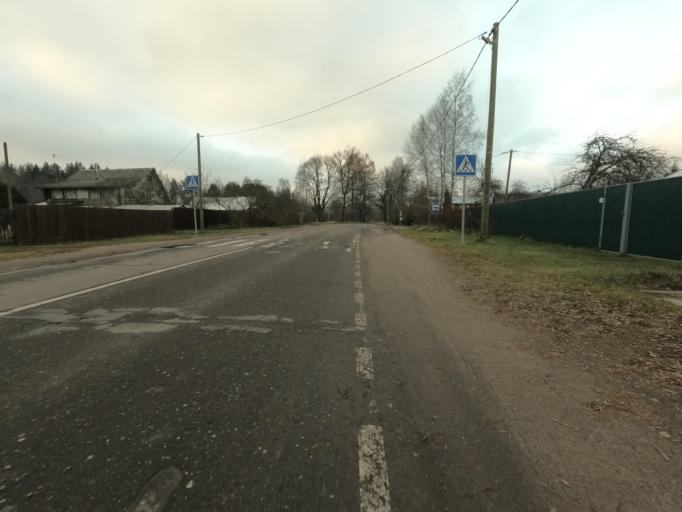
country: RU
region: Leningrad
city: Kirovsk
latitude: 59.8016
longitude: 30.9924
